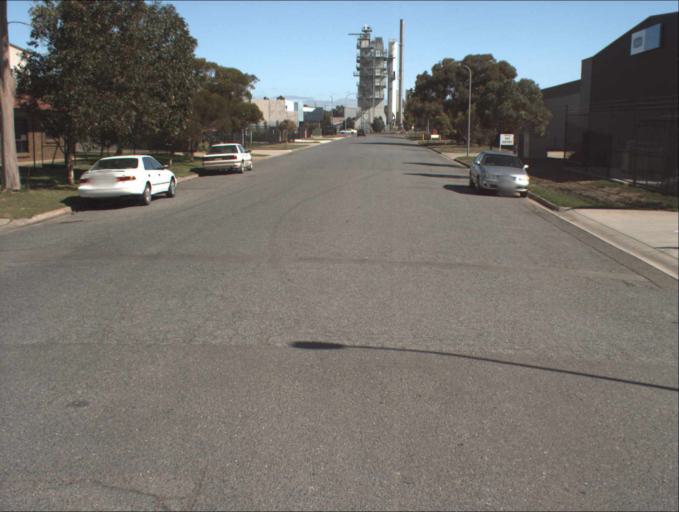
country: AU
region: South Australia
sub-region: Port Adelaide Enfield
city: Blair Athol
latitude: -34.8447
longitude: 138.5721
